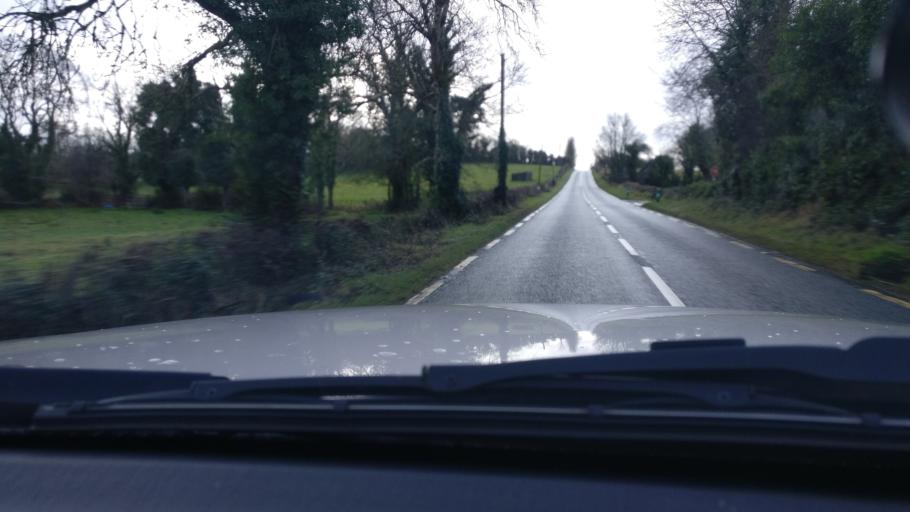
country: IE
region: Leinster
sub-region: An Iarmhi
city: Moate
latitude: 53.6211
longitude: -7.7000
